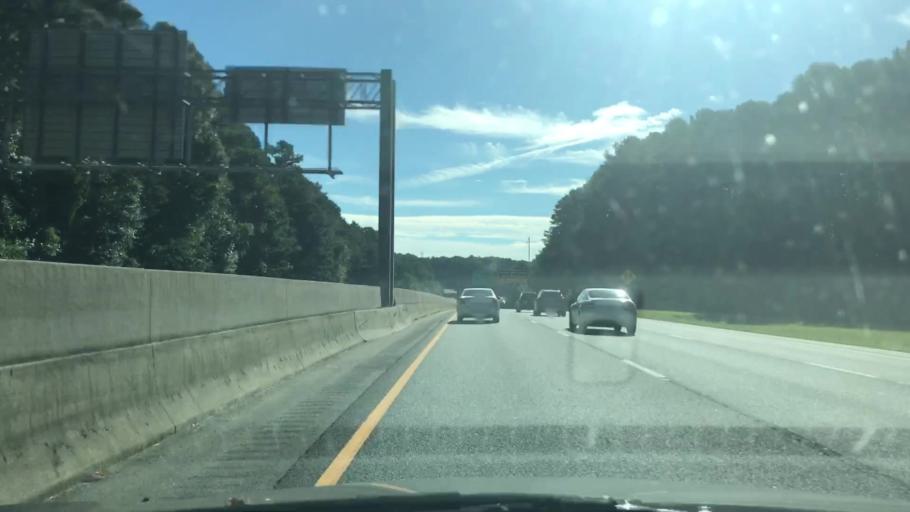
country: US
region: Georgia
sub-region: Gwinnett County
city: Mountain Park
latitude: 33.8239
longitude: -84.1460
